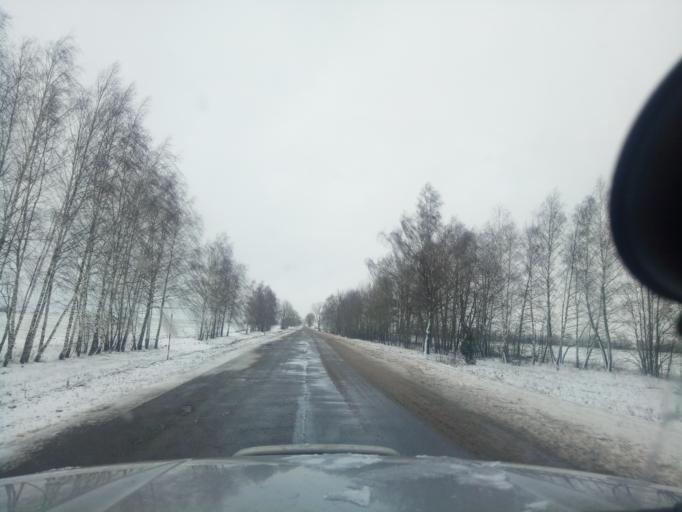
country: BY
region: Minsk
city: Tsimkavichy
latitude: 53.0541
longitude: 26.9169
